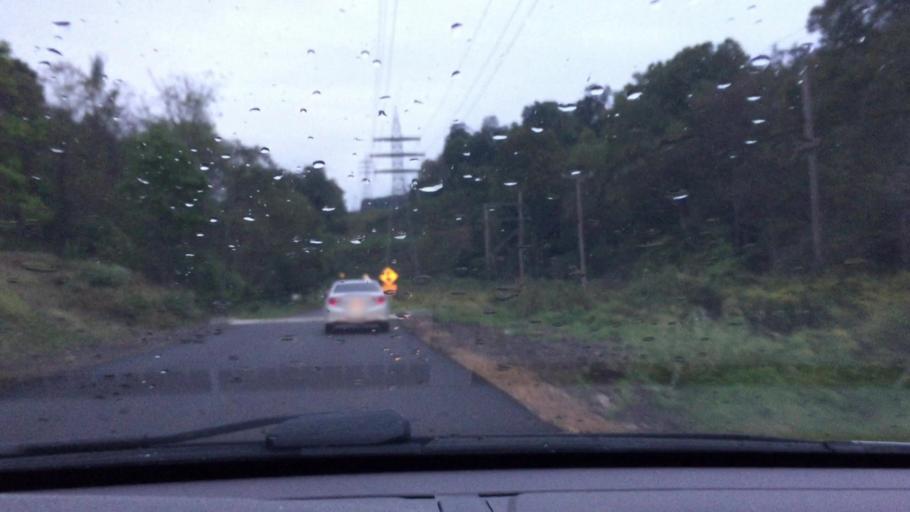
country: US
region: Pennsylvania
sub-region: Allegheny County
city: Cheswick
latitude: 40.5612
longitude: -79.8342
